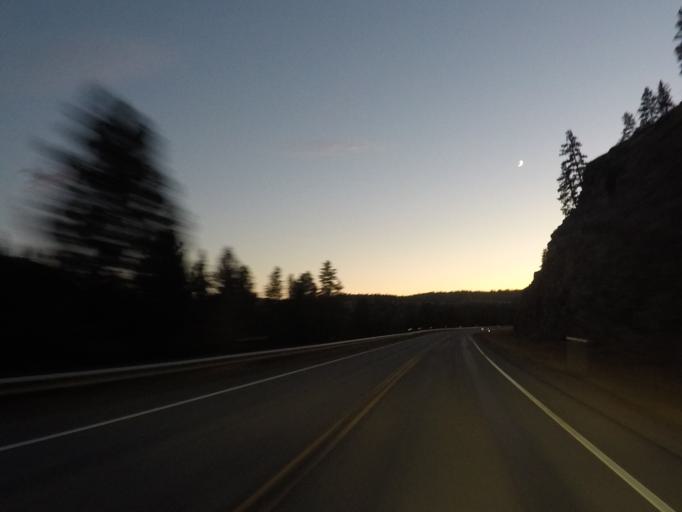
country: US
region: Montana
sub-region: Missoula County
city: Seeley Lake
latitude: 47.0150
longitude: -113.3218
